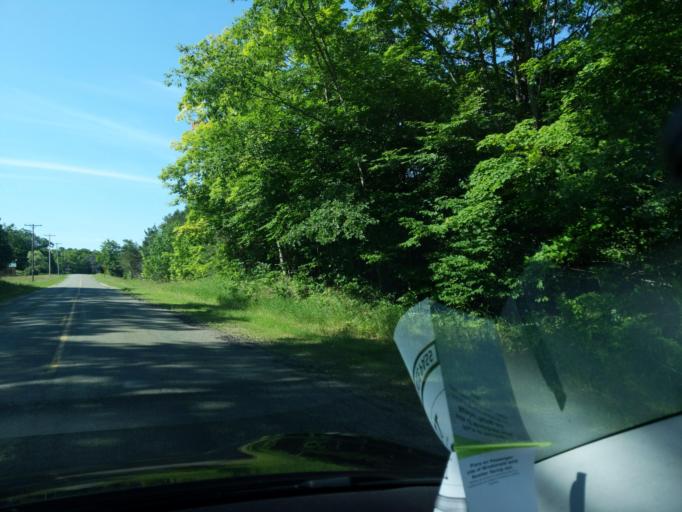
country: US
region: Michigan
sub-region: Mackinac County
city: Saint Ignace
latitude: 45.7026
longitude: -84.7316
